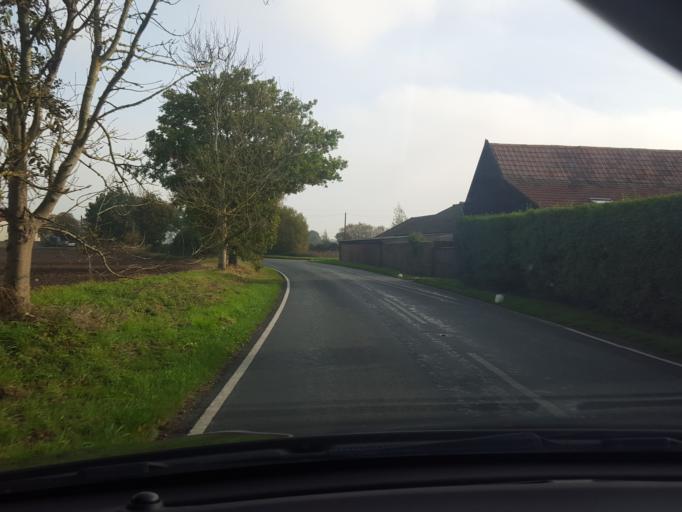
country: GB
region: England
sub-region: Essex
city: Mistley
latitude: 51.9299
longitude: 1.1450
